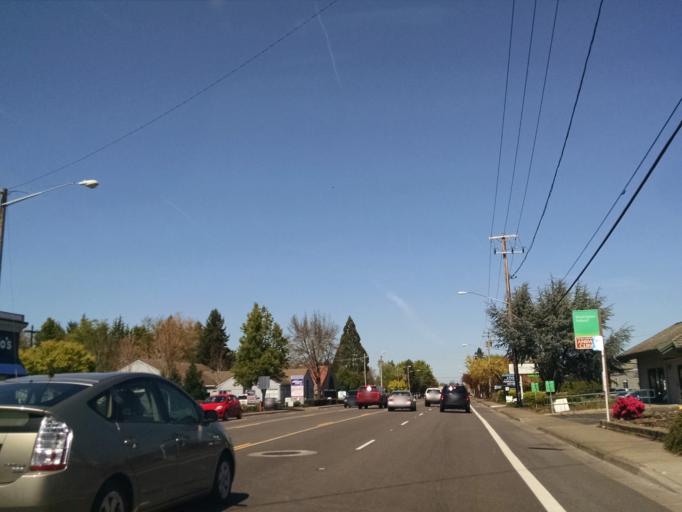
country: US
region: Oregon
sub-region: Lane County
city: Eugene
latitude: 44.0812
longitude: -123.0674
